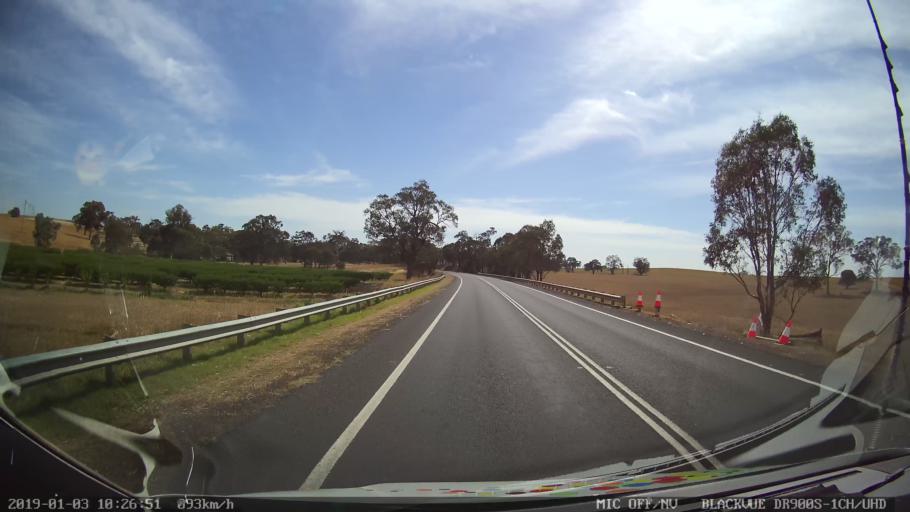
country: AU
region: New South Wales
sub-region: Young
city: Young
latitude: -34.4086
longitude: 148.2538
